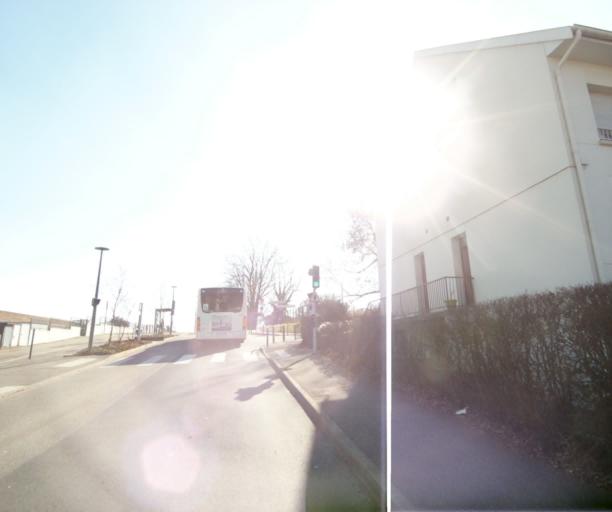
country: FR
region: Lorraine
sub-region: Departement de Meurthe-et-Moselle
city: Vandoeuvre-les-Nancy
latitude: 48.6525
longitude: 6.1758
